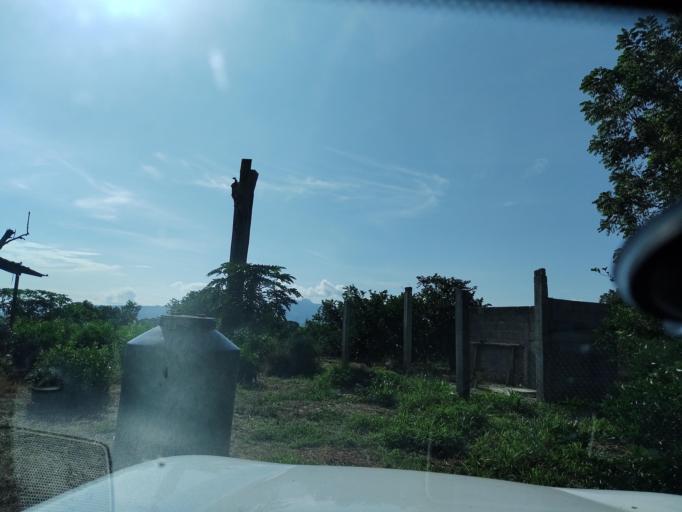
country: MX
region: Veracruz
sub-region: Misantla
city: La Defensa
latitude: 20.1102
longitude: -96.9875
